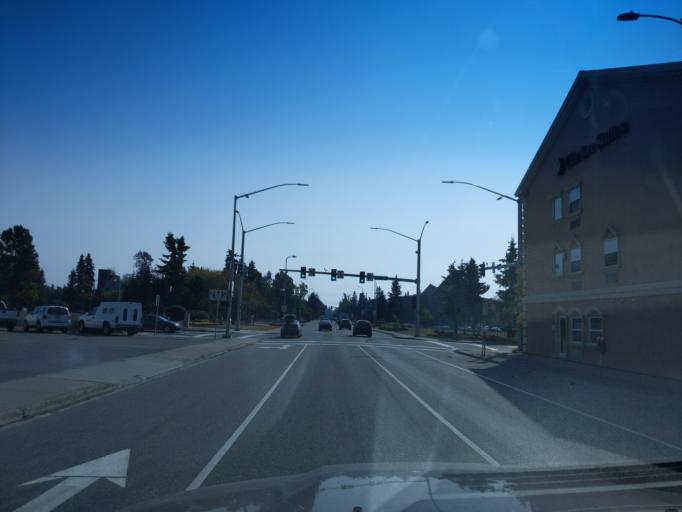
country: US
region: Alaska
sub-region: Anchorage Municipality
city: Anchorage
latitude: 61.2141
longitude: -149.9037
